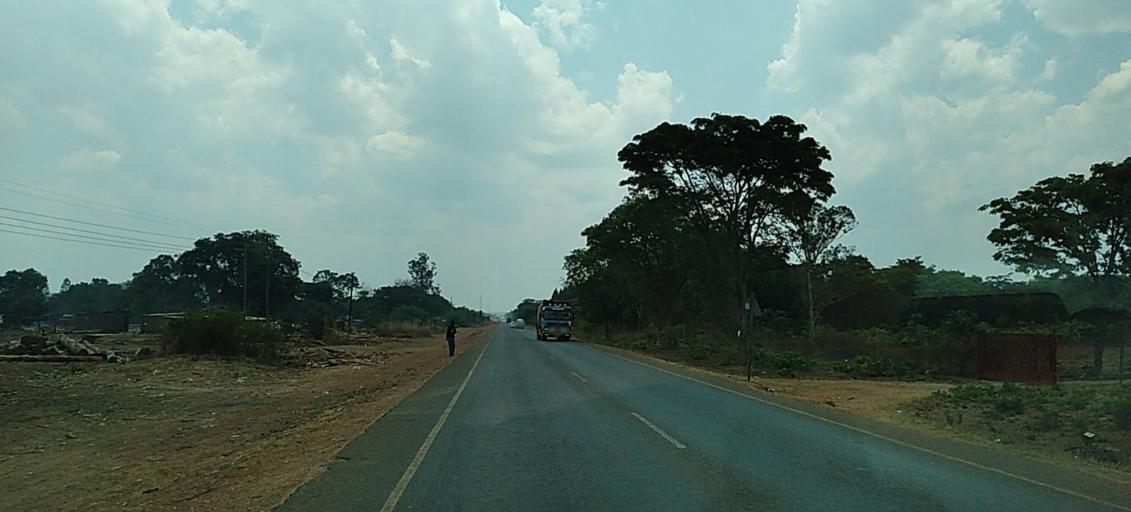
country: ZM
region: Copperbelt
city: Kalulushi
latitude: -12.8438
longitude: 28.0114
